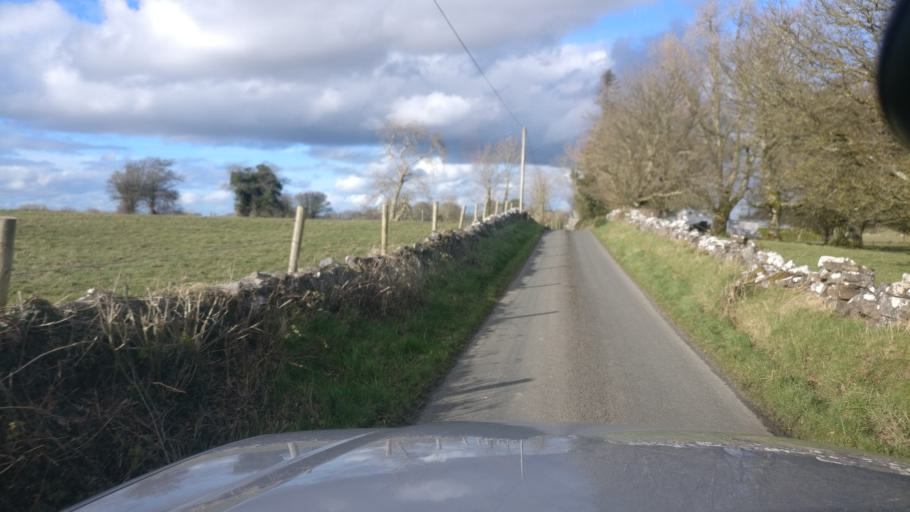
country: IE
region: Connaught
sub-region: County Galway
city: Loughrea
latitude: 53.1746
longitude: -8.4270
